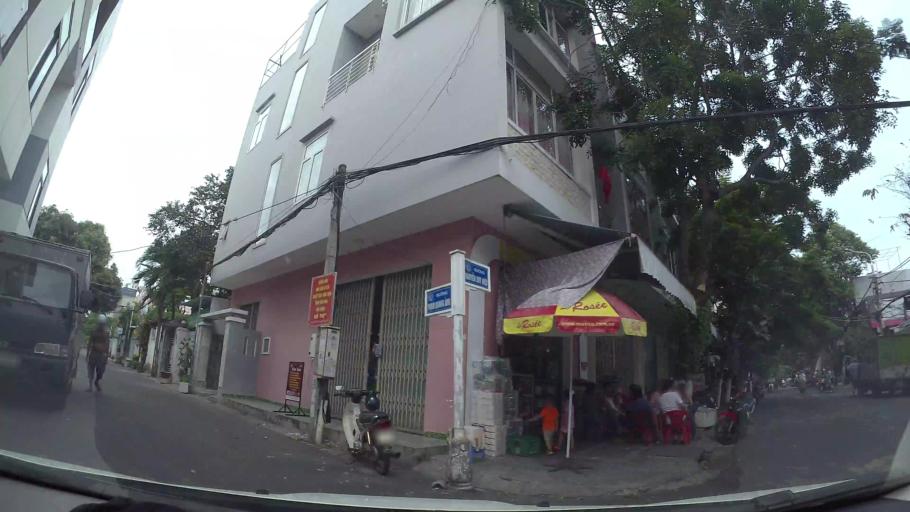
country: VN
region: Da Nang
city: Son Tra
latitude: 16.0552
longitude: 108.2371
